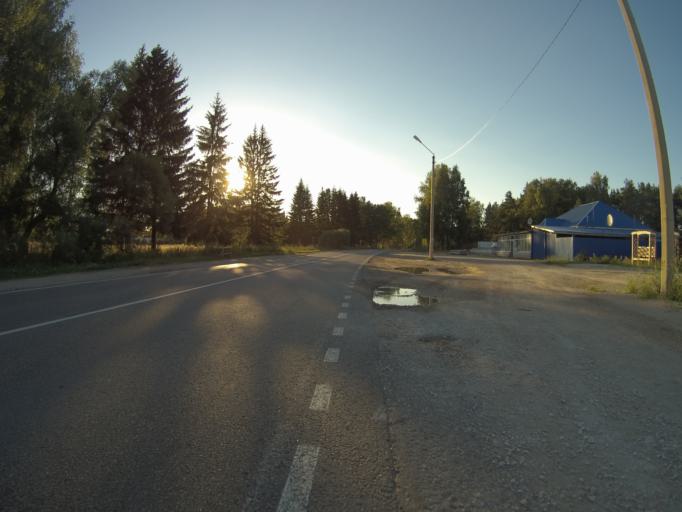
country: RU
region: Vladimir
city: Anopino
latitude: 55.7071
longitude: 40.7330
